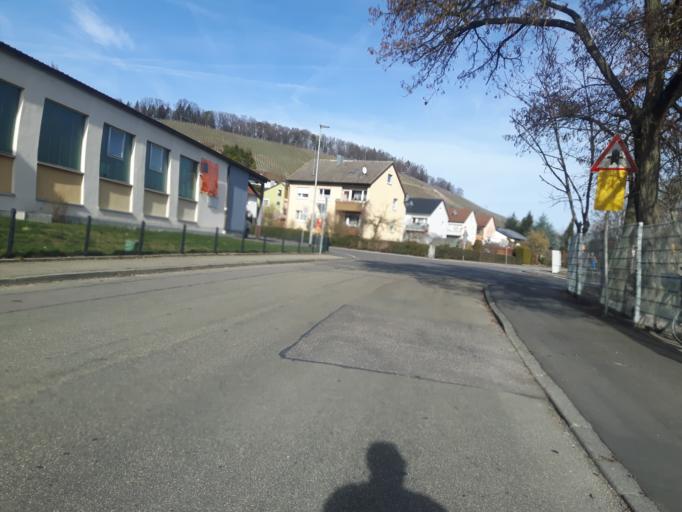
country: DE
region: Baden-Wuerttemberg
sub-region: Regierungsbezirk Stuttgart
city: Lowenstein
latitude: 49.1382
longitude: 9.3844
